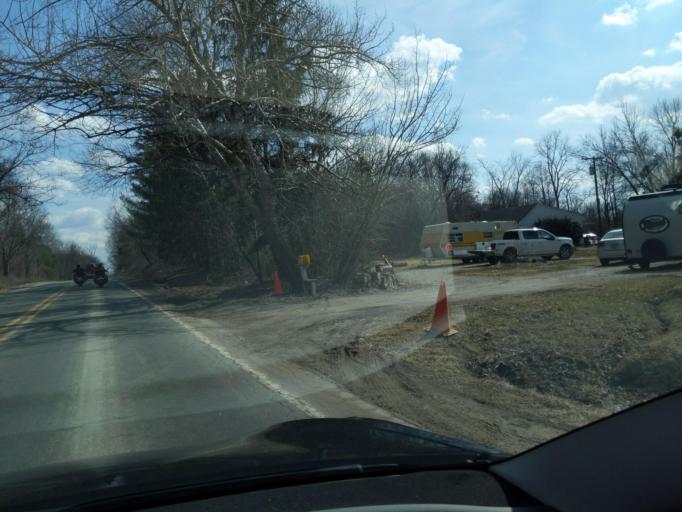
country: US
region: Michigan
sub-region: Livingston County
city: Whitmore Lake
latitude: 42.3795
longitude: -83.7826
